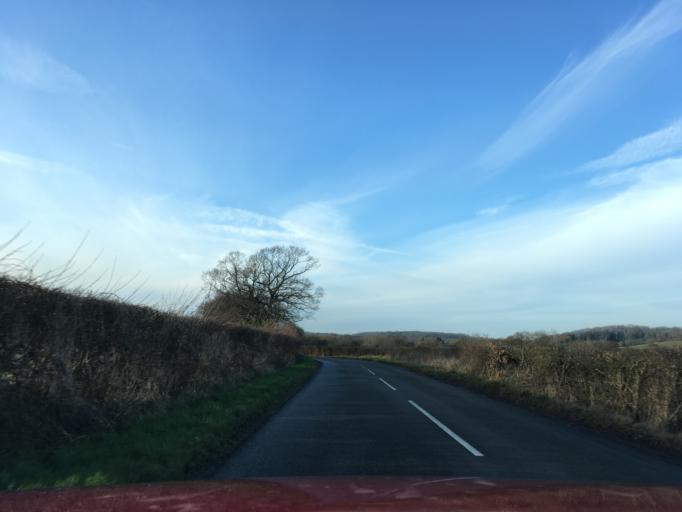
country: GB
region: England
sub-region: Warwickshire
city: Henley in Arden
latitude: 52.2457
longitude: -1.7878
